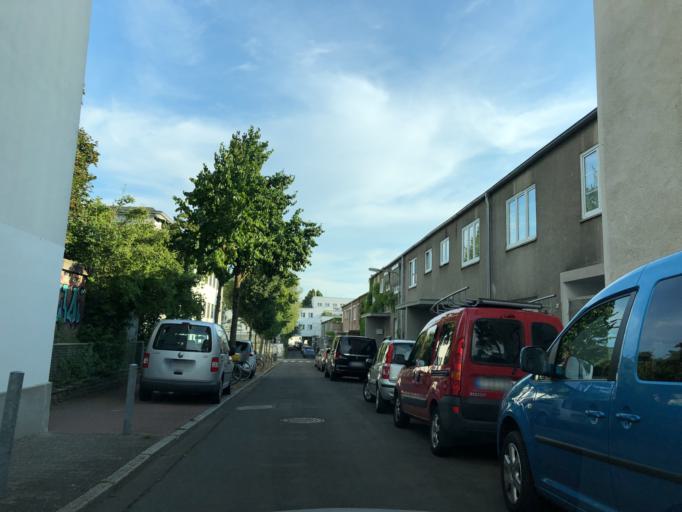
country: DE
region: Hesse
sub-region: Regierungsbezirk Darmstadt
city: Frankfurt am Main
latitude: 50.1288
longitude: 8.7178
